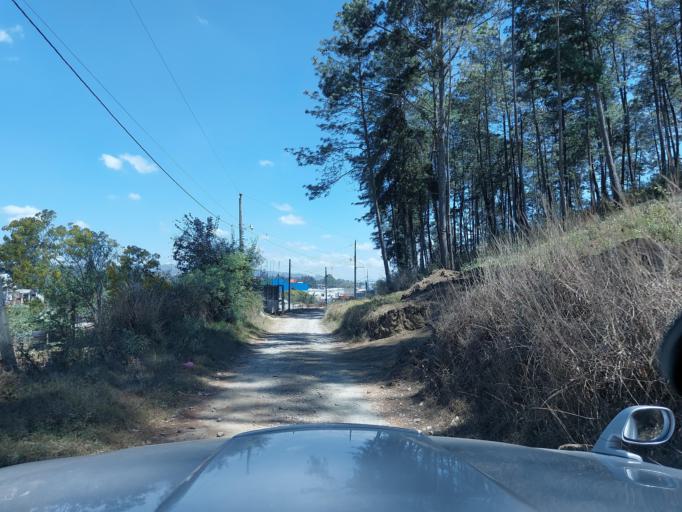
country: GT
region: Chimaltenango
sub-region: Municipio de Chimaltenango
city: Chimaltenango
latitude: 14.6528
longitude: -90.8314
